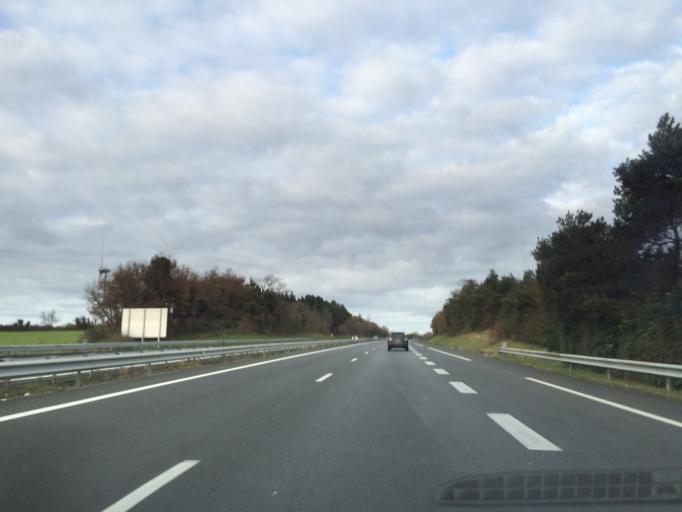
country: FR
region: Poitou-Charentes
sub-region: Departement de la Charente-Maritime
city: Saint-Jean-d'Angely
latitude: 46.0162
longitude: -0.5413
